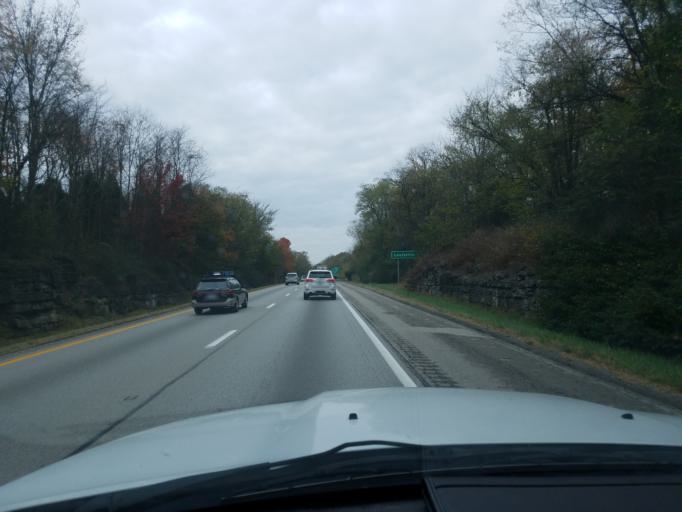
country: US
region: Kentucky
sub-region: Oldham County
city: Orchard Grass Hills
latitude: 38.3342
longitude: -85.5338
